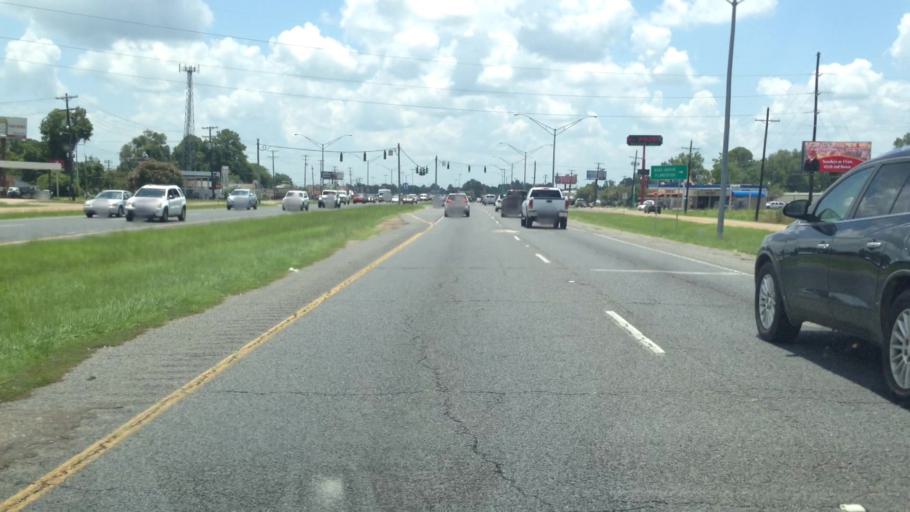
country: US
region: Louisiana
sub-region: Rapides Parish
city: Alexandria
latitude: 31.3065
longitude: -92.4797
